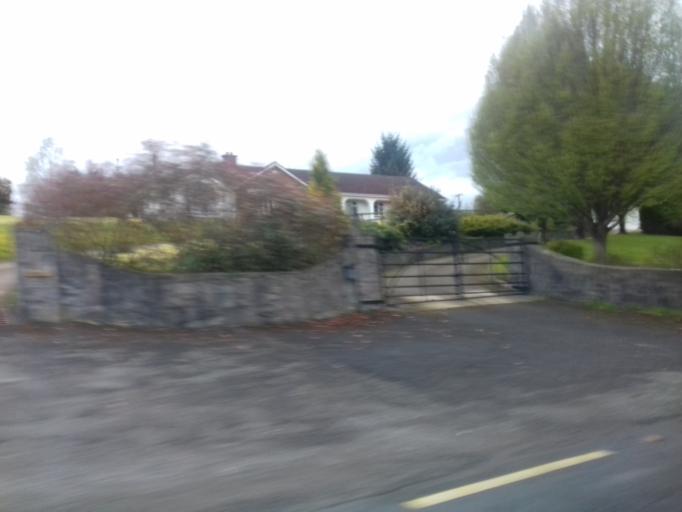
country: IE
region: Ulster
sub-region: An Cabhan
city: Ballyconnell
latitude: 54.0882
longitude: -7.5362
